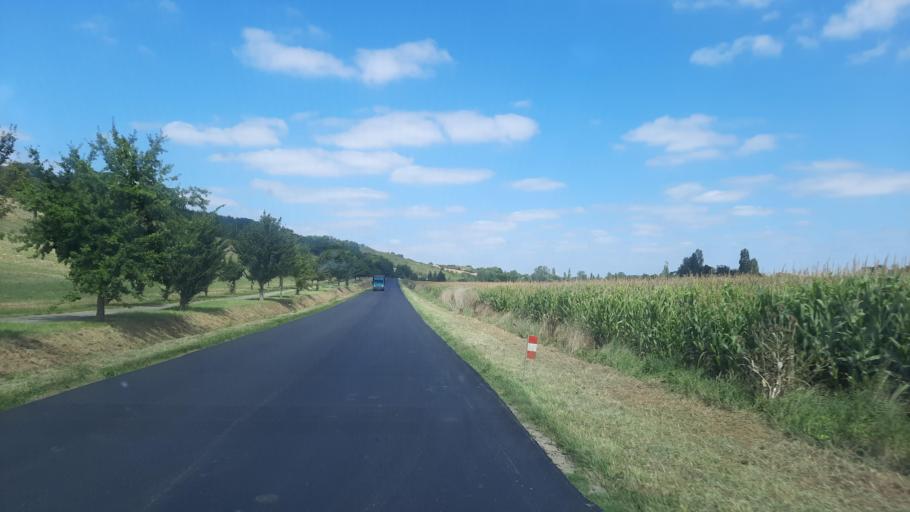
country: FR
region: Midi-Pyrenees
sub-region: Departement du Gers
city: Lombez
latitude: 43.4651
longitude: 0.8910
